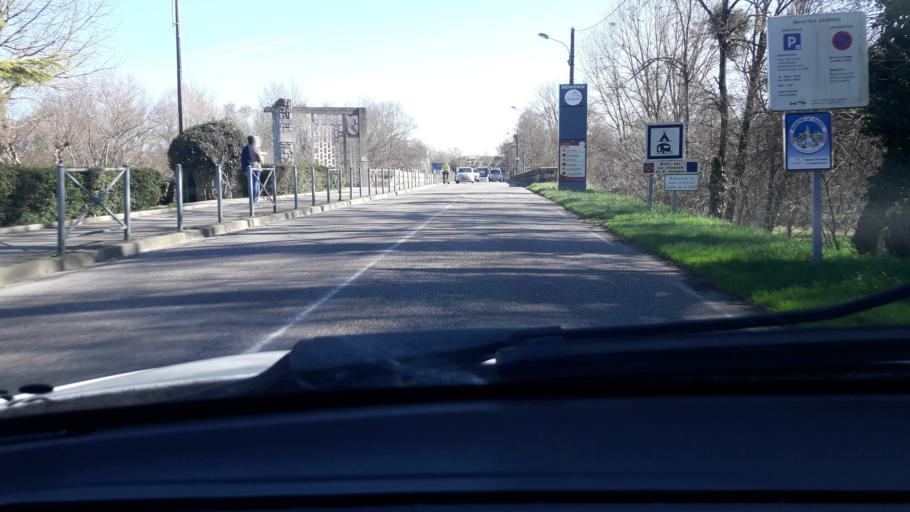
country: FR
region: Midi-Pyrenees
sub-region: Departement du Gers
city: Pujaudran
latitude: 43.6144
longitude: 1.0743
